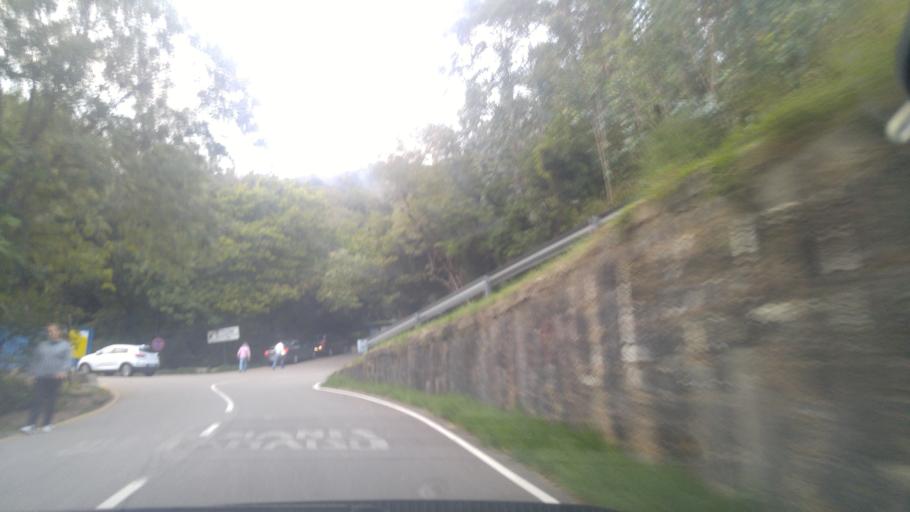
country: ES
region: Asturias
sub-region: Province of Asturias
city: Oviedo
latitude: 43.3802
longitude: -5.8676
